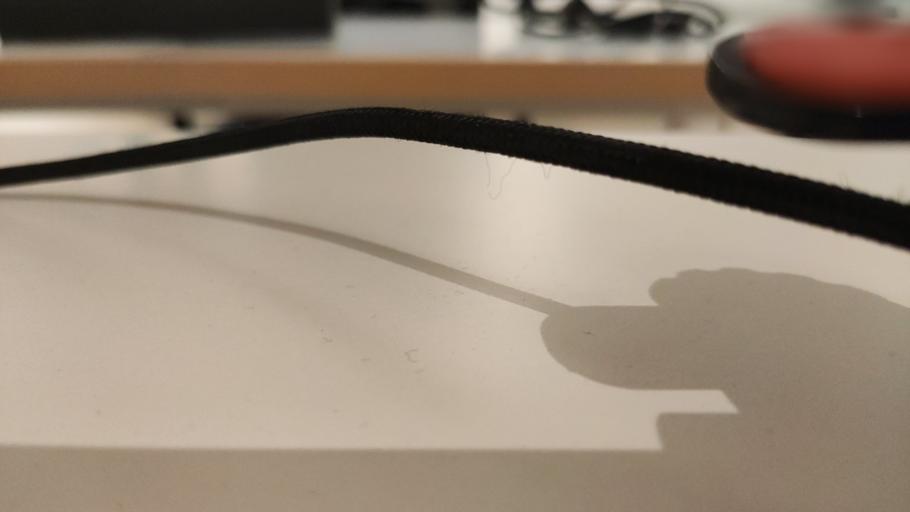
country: RU
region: Moskovskaya
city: Dorokhovo
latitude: 55.3852
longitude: 36.3970
